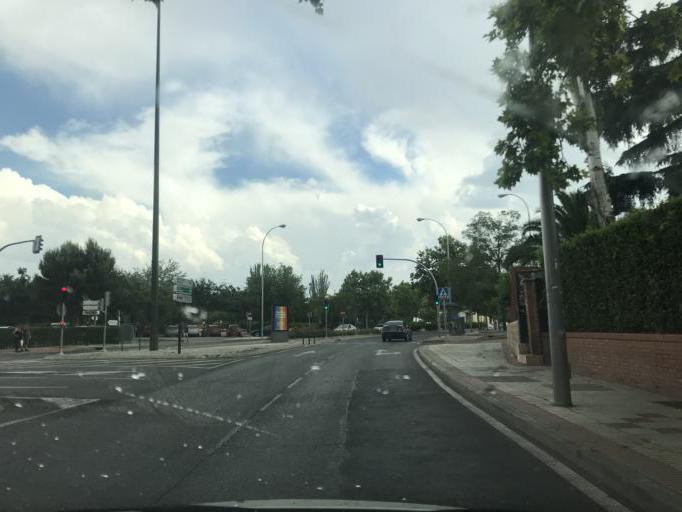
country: ES
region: Madrid
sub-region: Provincia de Madrid
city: Barajas de Madrid
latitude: 40.4695
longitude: -3.5815
